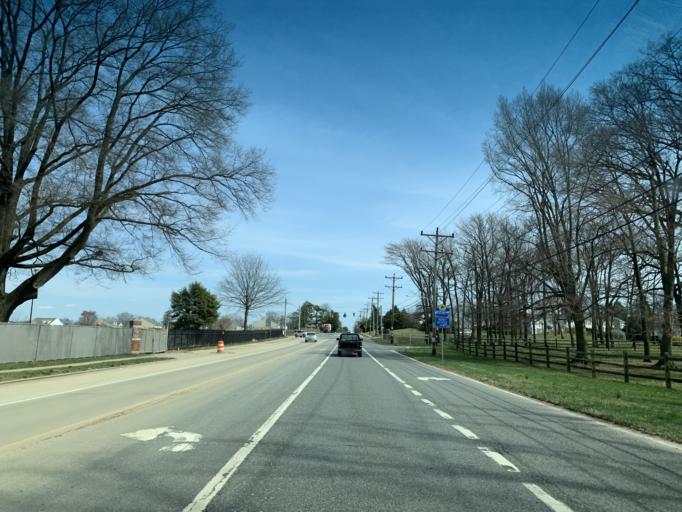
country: US
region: Delaware
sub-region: New Castle County
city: Newport
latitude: 39.7254
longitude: -75.6119
